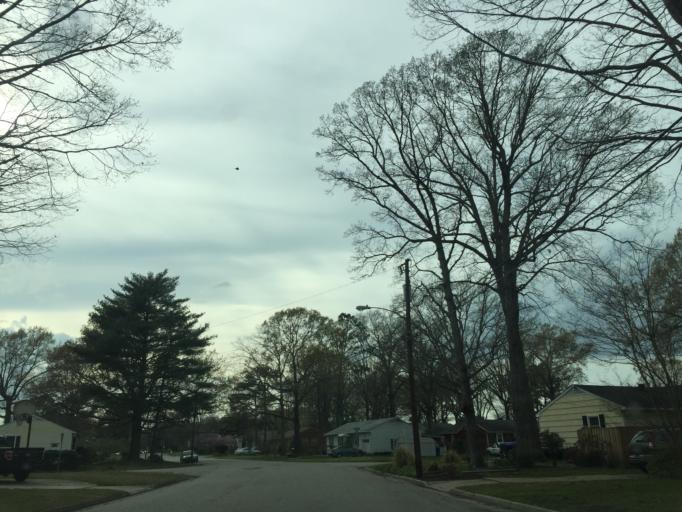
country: US
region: Virginia
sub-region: City of Newport News
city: Newport News
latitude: 37.0774
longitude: -76.4538
